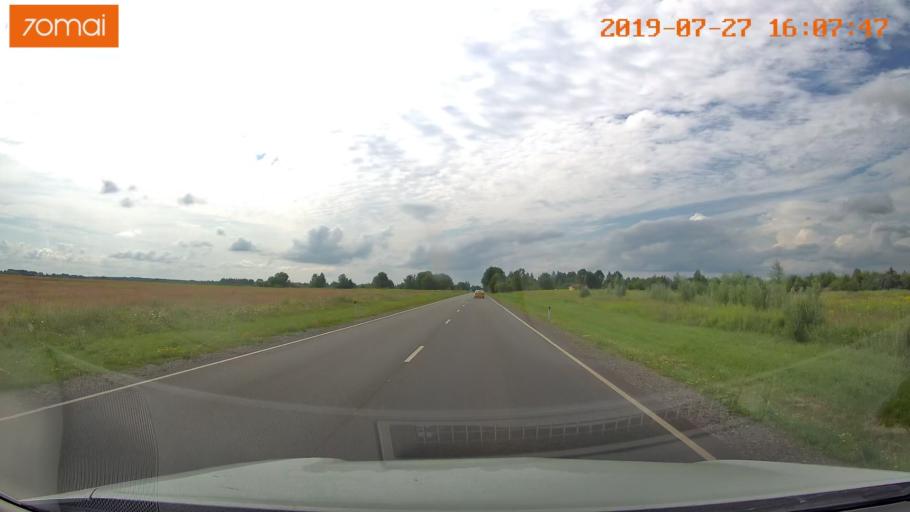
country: RU
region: Kaliningrad
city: Chernyakhovsk
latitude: 54.6358
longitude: 21.7497
